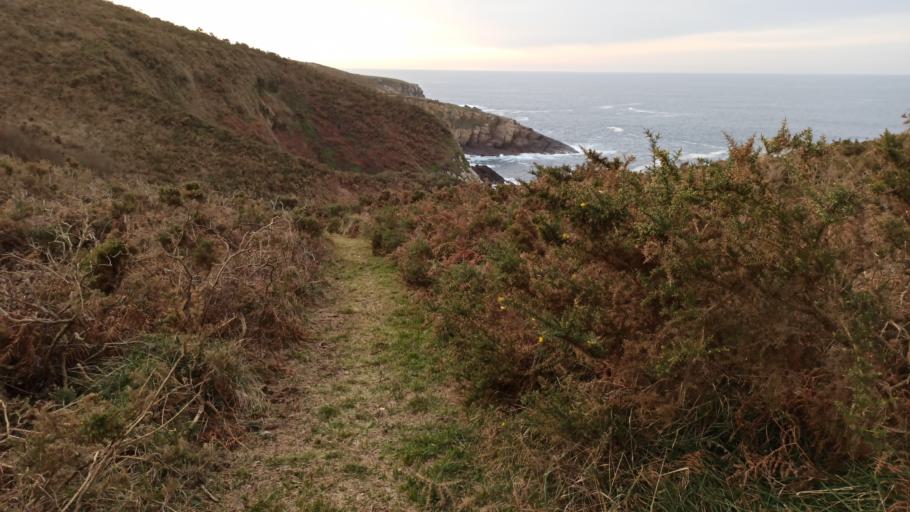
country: ES
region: Galicia
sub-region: Provincia da Coruna
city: A Coruna
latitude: 43.3981
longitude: -8.3351
